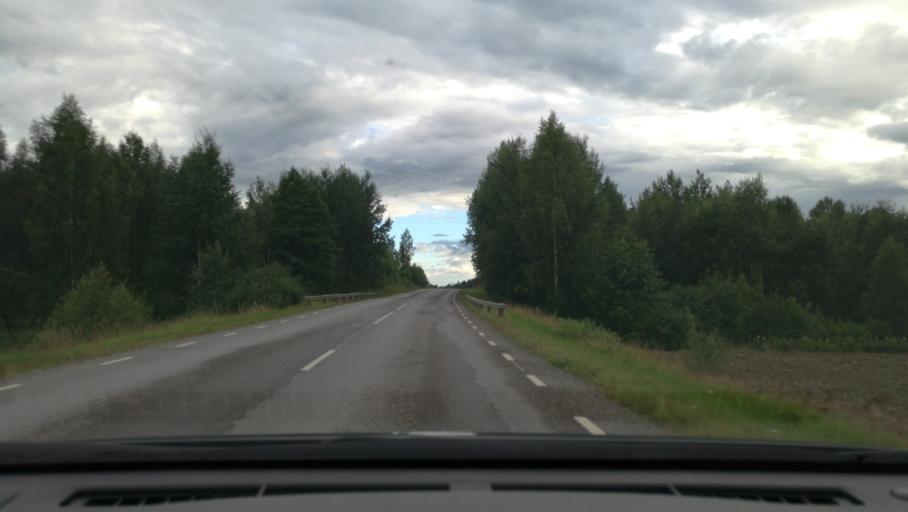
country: SE
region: OEstergoetland
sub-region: Norrkopings Kommun
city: Svartinge
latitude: 58.7143
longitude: 15.9381
